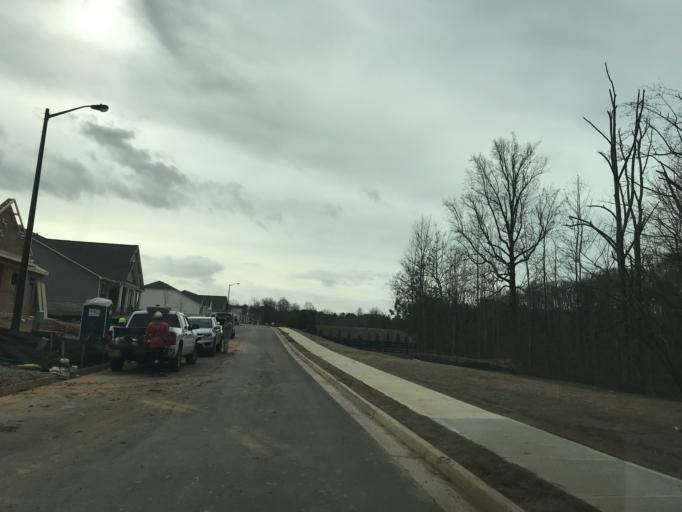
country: US
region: Georgia
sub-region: Cherokee County
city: Canton
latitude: 34.1992
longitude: -84.4012
